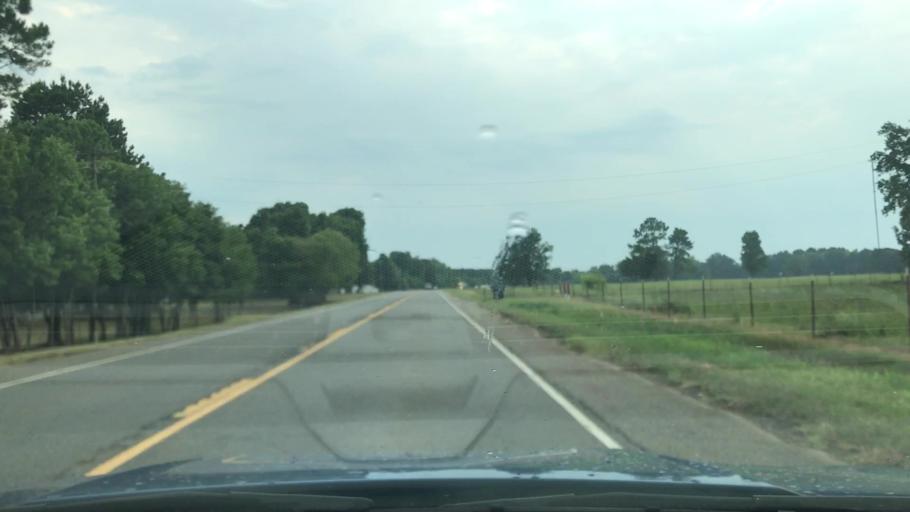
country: US
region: Texas
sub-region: Harrison County
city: Waskom
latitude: 32.4597
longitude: -94.0227
